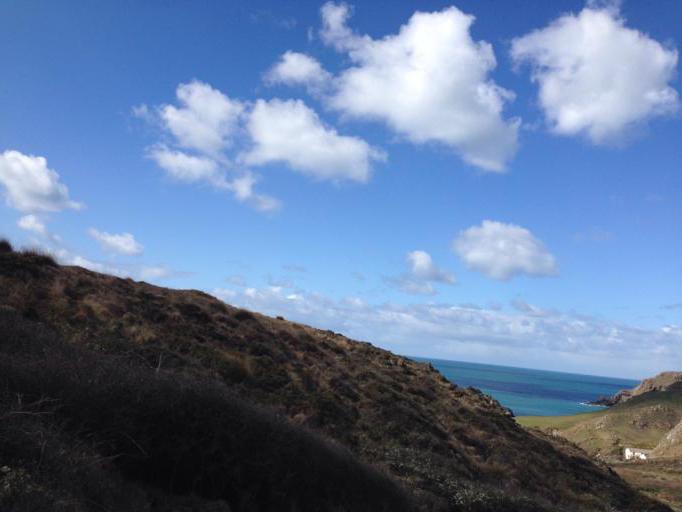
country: GB
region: England
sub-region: Cornwall
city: Landewednack
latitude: 49.9754
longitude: -5.2260
